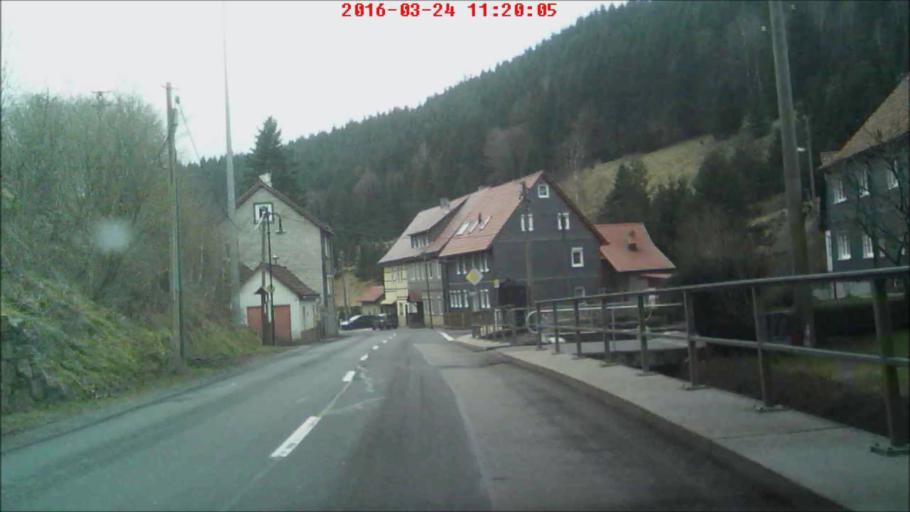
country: DE
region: Thuringia
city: Eisfeld
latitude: 50.4926
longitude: 10.9122
